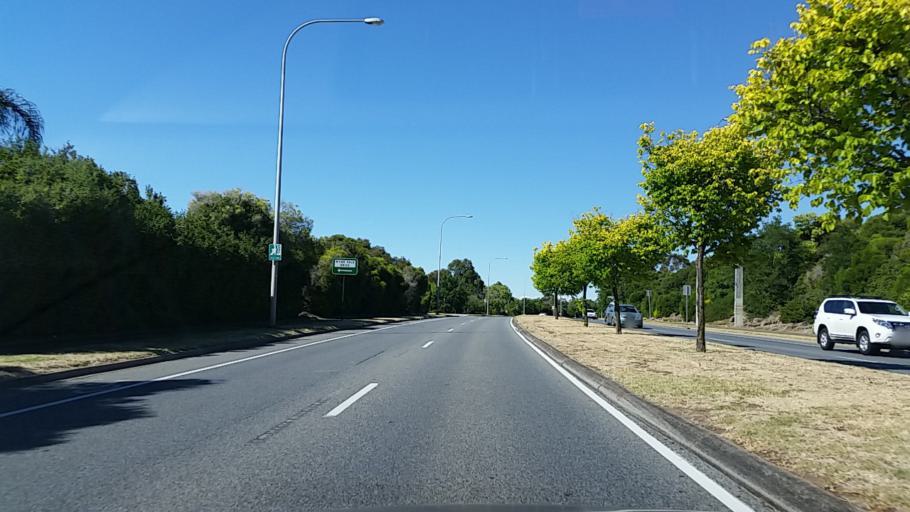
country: AU
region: South Australia
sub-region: Tea Tree Gully
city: Modbury
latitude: -34.7985
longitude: 138.6860
